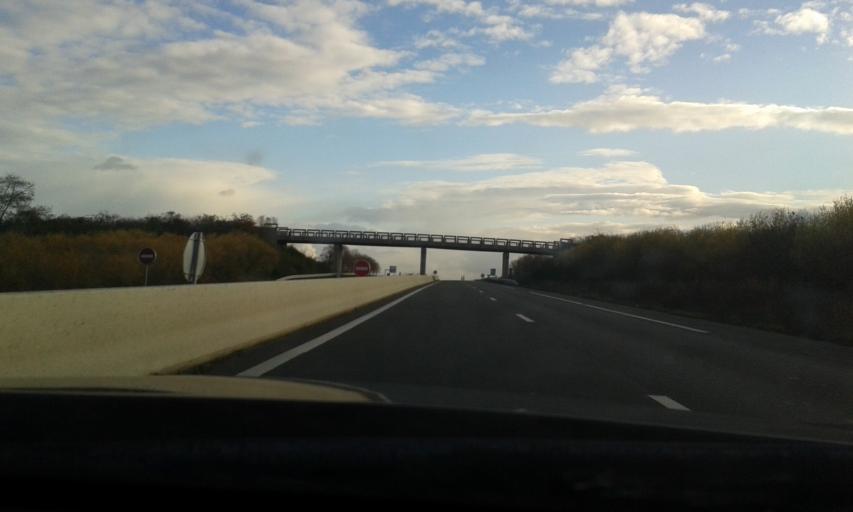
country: FR
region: Centre
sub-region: Departement d'Eure-et-Loir
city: Leves
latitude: 48.5085
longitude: 1.4630
